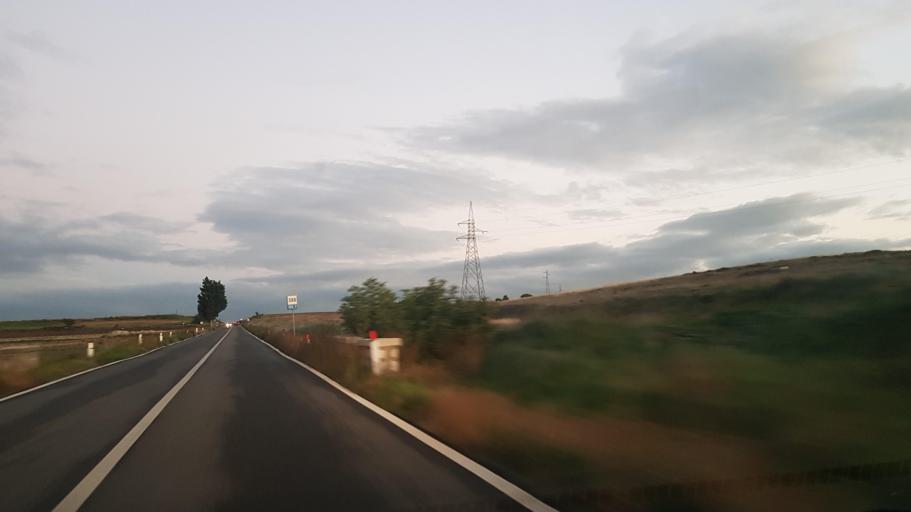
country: IT
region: Basilicate
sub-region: Provincia di Matera
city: Matera
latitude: 40.6742
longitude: 16.6824
